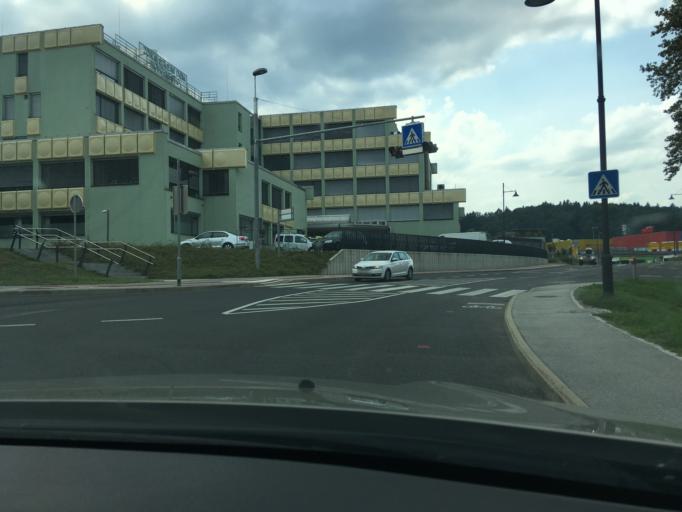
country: SI
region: Novo Mesto
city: Novo Mesto
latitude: 45.8014
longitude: 15.1636
